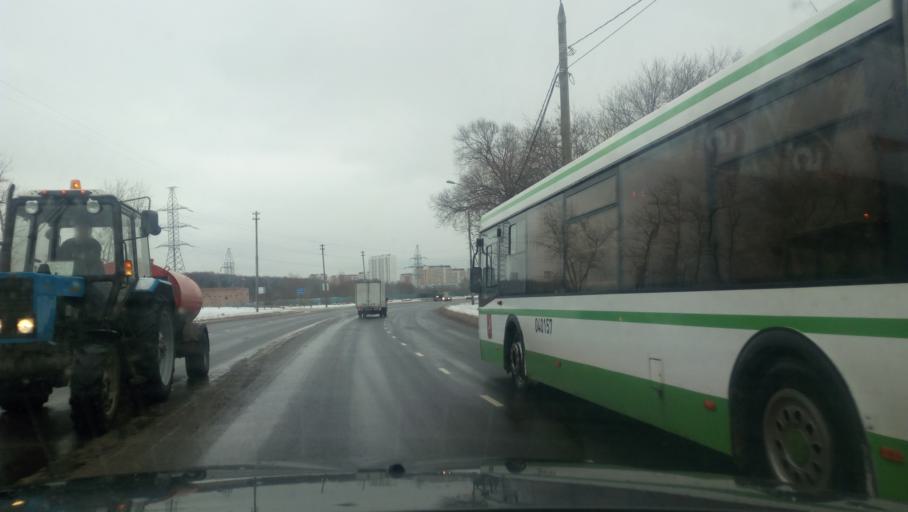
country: RU
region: Moscow
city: Zhulebino
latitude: 55.7209
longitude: 37.8675
